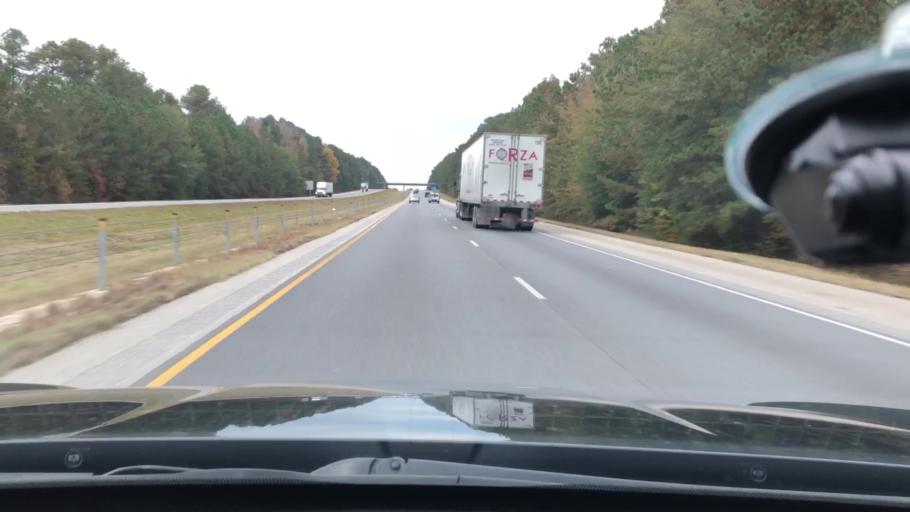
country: US
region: Arkansas
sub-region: Clark County
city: Arkadelphia
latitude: 34.0867
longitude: -93.1117
